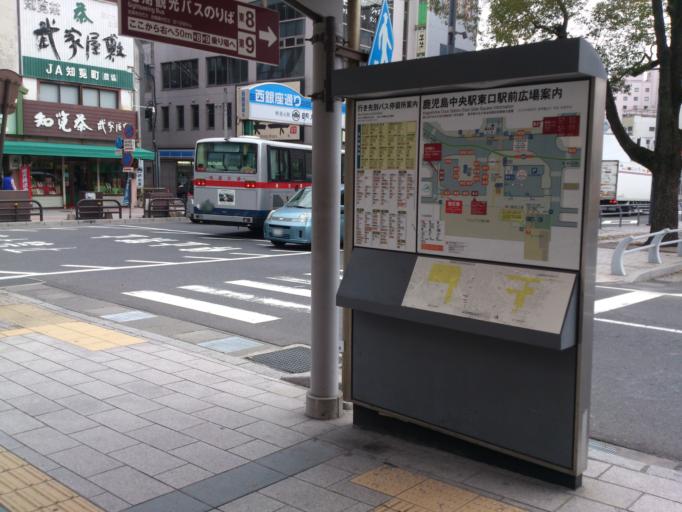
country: JP
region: Kagoshima
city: Kagoshima-shi
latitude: 31.5850
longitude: 130.5433
